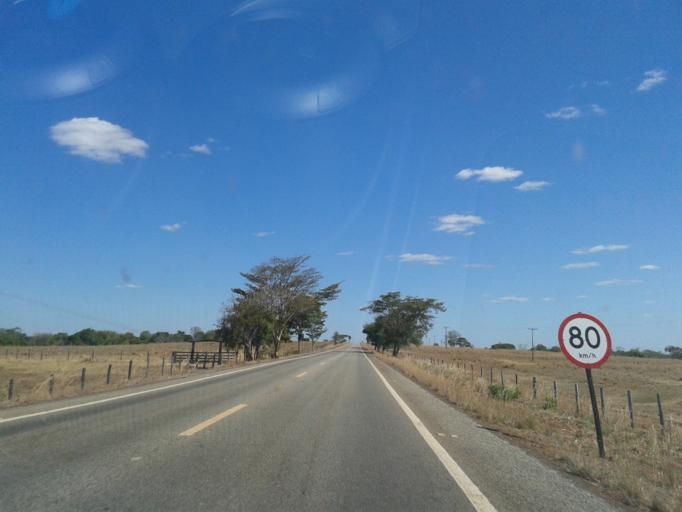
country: BR
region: Goias
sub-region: Sao Miguel Do Araguaia
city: Sao Miguel do Araguaia
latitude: -13.4098
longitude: -50.2652
